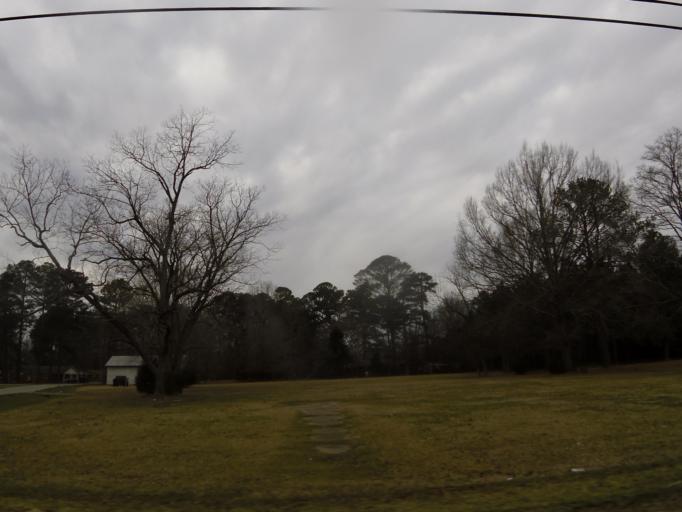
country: US
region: North Carolina
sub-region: Northampton County
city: Jackson
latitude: 36.2757
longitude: -77.2839
